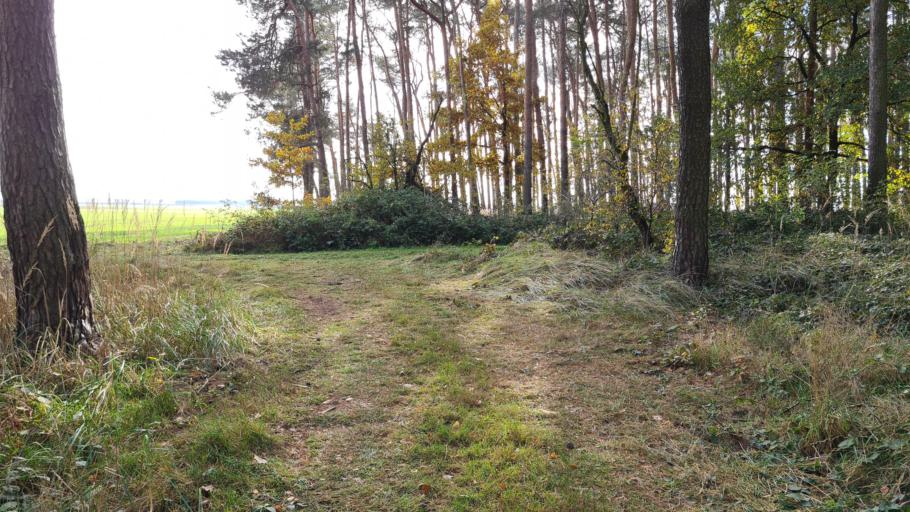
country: DE
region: Saxony-Anhalt
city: Zahna
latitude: 51.9671
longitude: 12.8355
